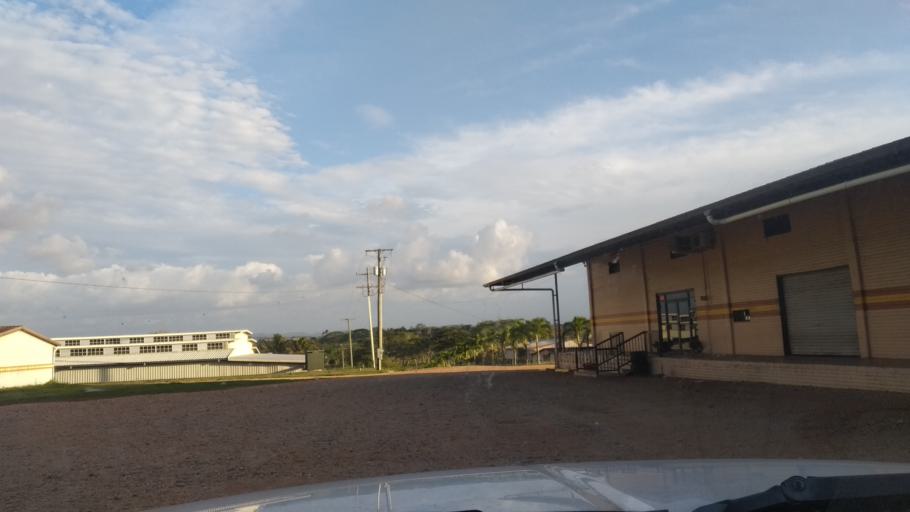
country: BZ
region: Cayo
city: San Ignacio
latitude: 17.2581
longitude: -88.9926
